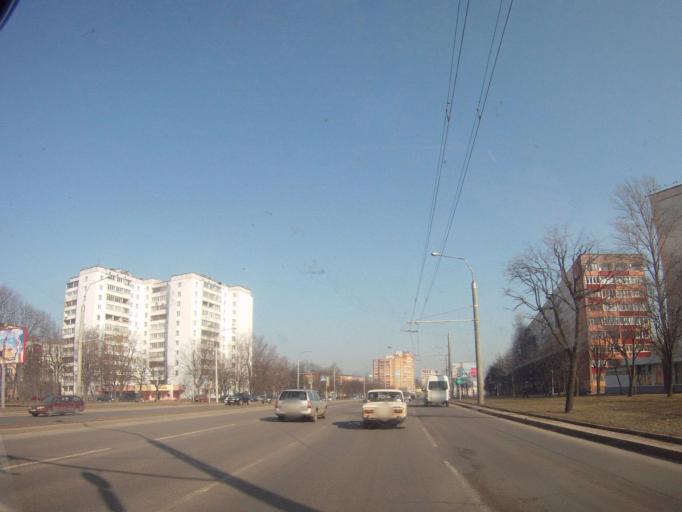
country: BY
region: Minsk
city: Novoye Medvezhino
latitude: 53.9170
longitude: 27.4958
